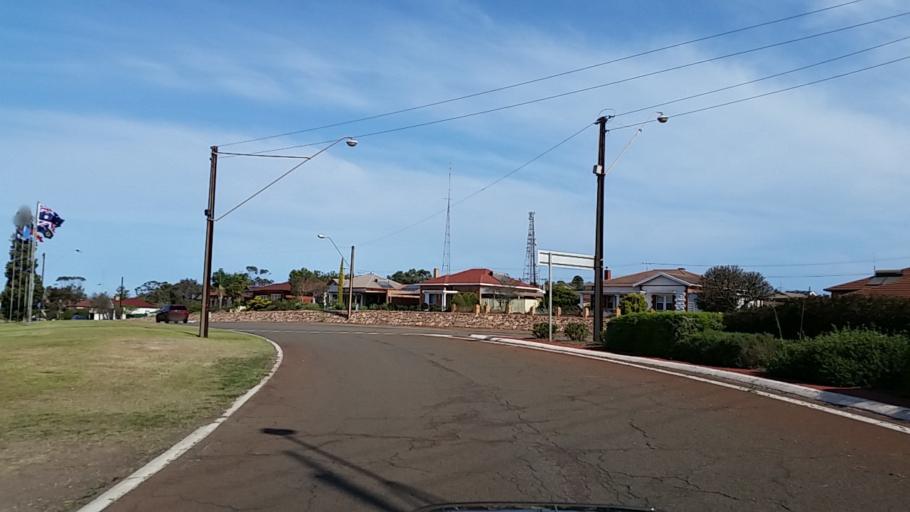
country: AU
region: South Australia
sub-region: Whyalla
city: Whyalla
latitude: -33.0251
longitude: 137.5724
